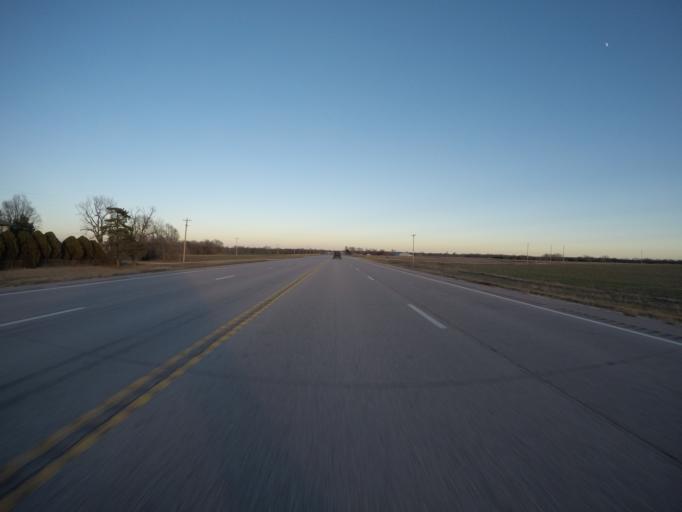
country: US
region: Kansas
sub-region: Marion County
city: Peabody
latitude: 38.1746
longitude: -97.1362
